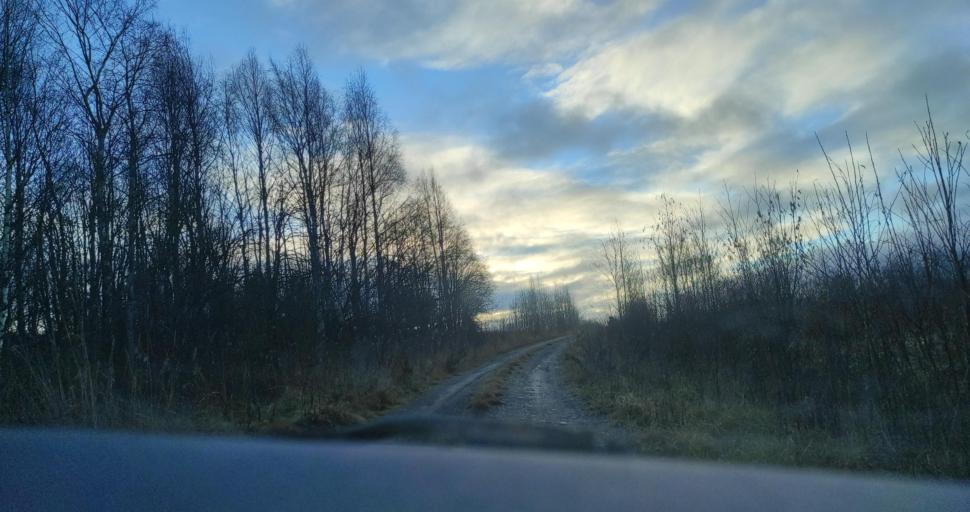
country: RU
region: Republic of Karelia
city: Pitkyaranta
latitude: 61.7284
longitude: 31.3822
